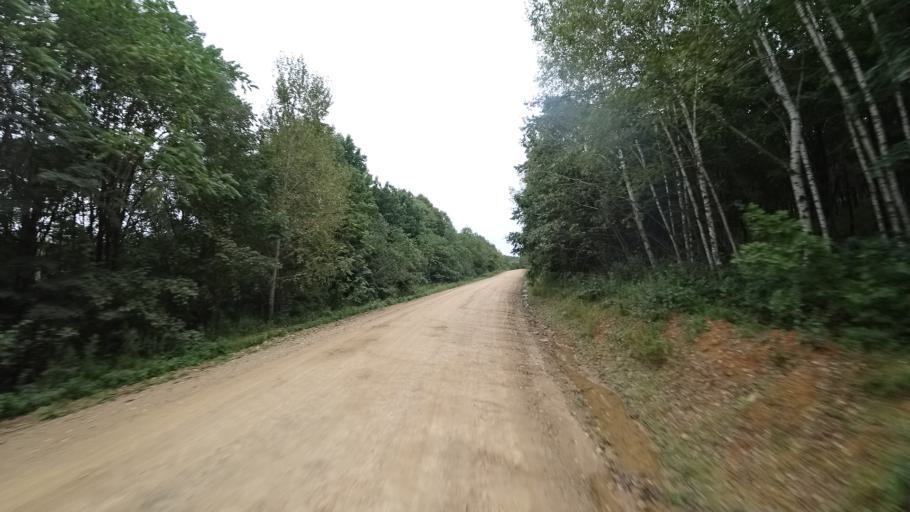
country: RU
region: Primorskiy
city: Rettikhovka
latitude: 44.1835
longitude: 132.8059
